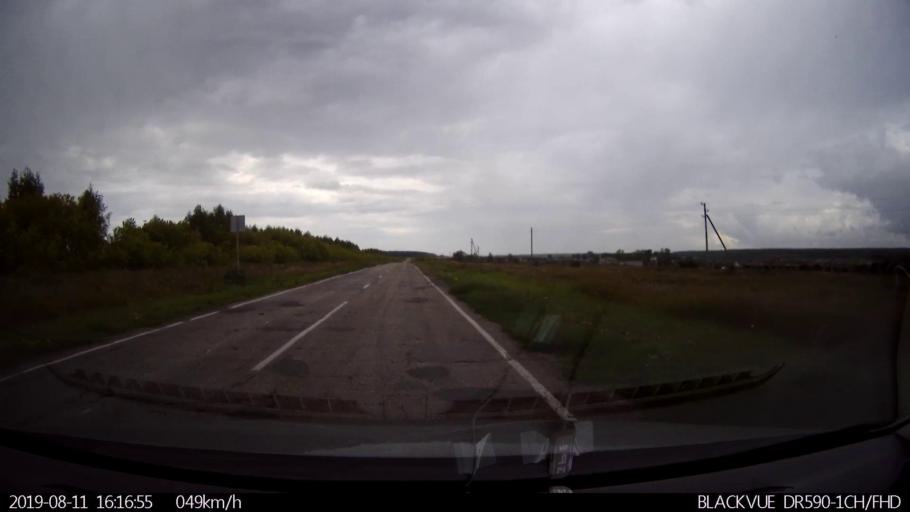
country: RU
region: Ulyanovsk
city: Mayna
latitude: 54.0445
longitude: 47.6190
